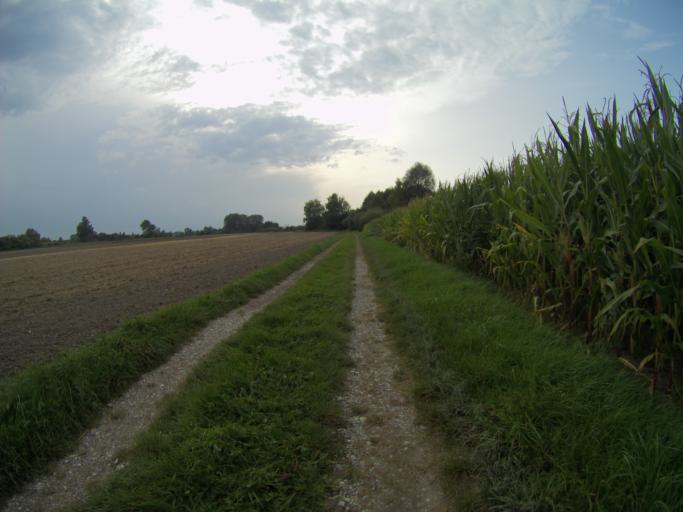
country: DE
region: Bavaria
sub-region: Upper Bavaria
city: Marzling
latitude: 48.3979
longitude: 11.7961
